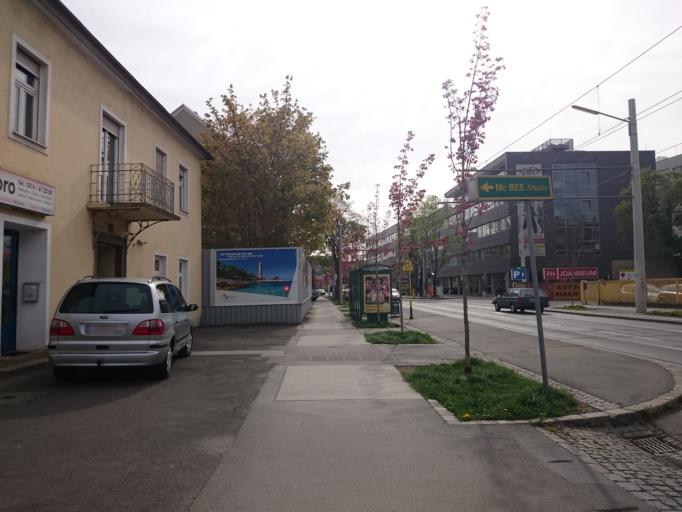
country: AT
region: Styria
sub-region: Graz Stadt
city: Wetzelsdorf
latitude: 47.0703
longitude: 15.4051
